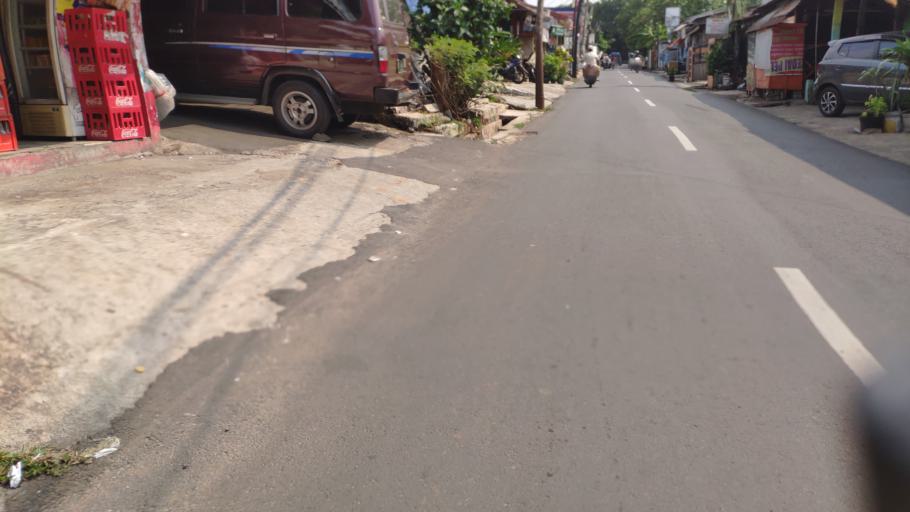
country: ID
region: West Java
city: Depok
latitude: -6.3181
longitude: 106.8191
